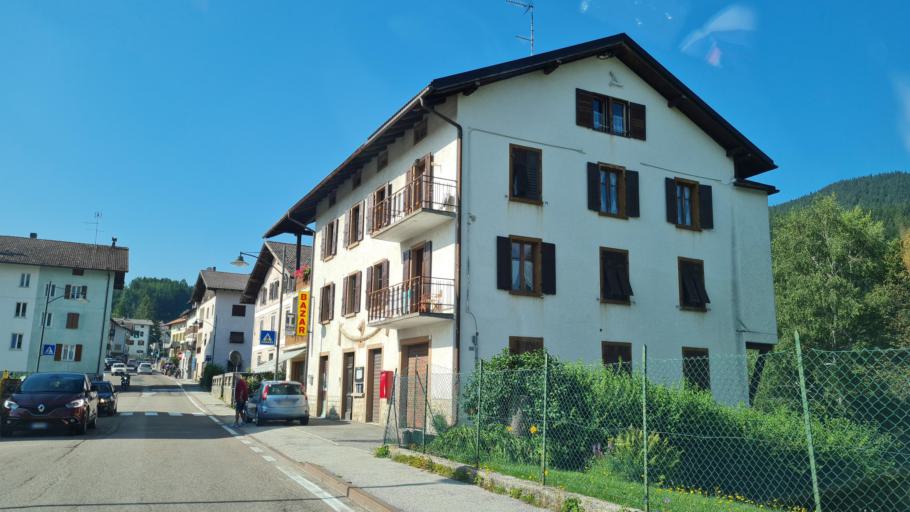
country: IT
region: Trentino-Alto Adige
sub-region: Provincia di Trento
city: Centa San Nicolo
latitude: 45.9359
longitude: 11.2270
